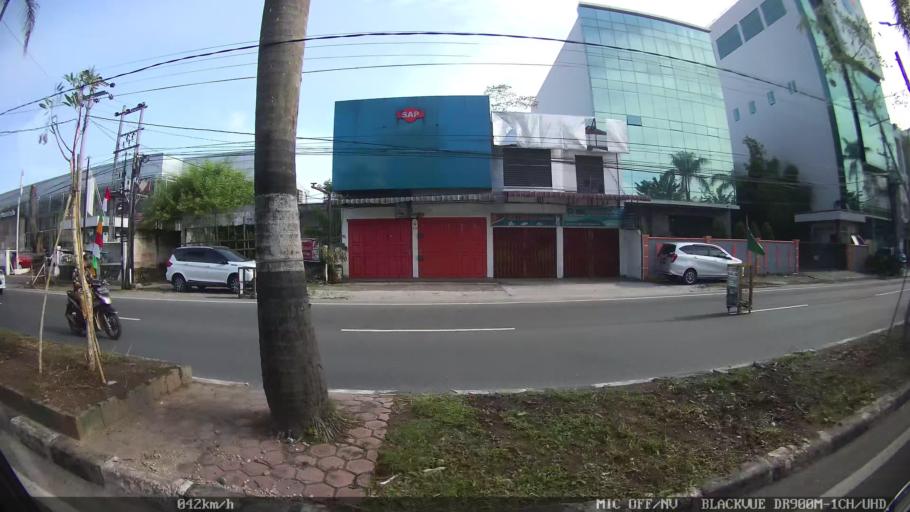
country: ID
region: North Sumatra
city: Medan
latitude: 3.6071
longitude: 98.6641
